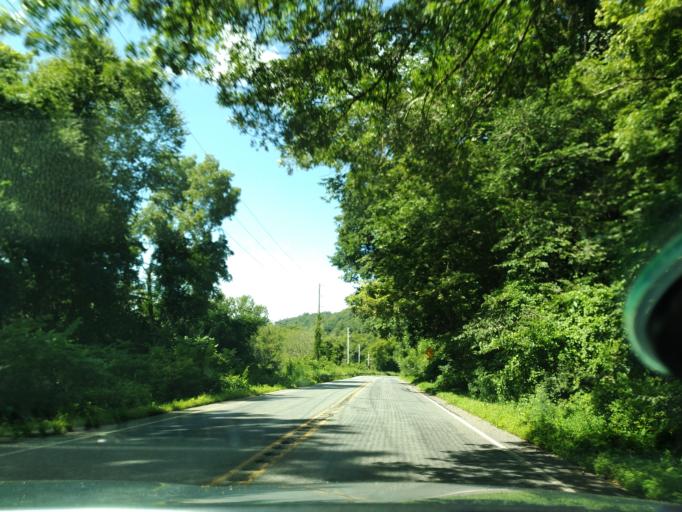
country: US
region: Pennsylvania
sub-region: Pike County
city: Pocono Ranch Lands
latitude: 41.1179
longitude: -74.9705
